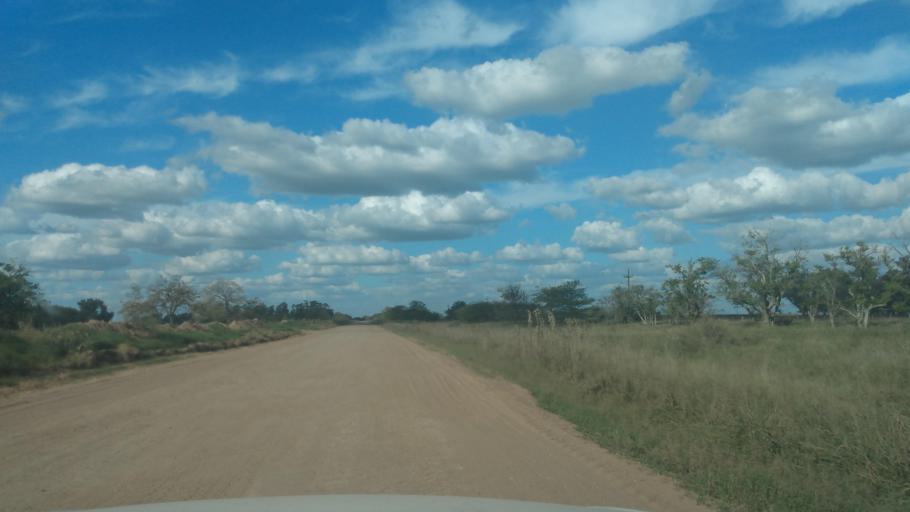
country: AR
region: Buenos Aires
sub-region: Partido de Navarro
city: Navarro
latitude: -35.0122
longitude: -59.4883
